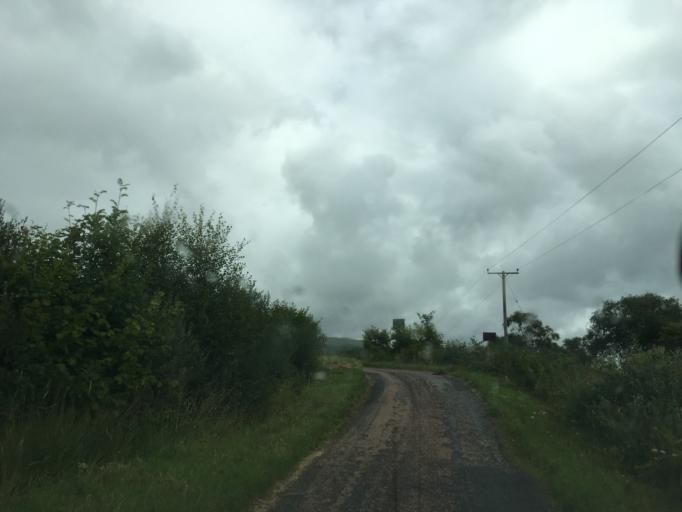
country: GB
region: Scotland
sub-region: Argyll and Bute
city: Oban
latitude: 56.2737
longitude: -5.3660
